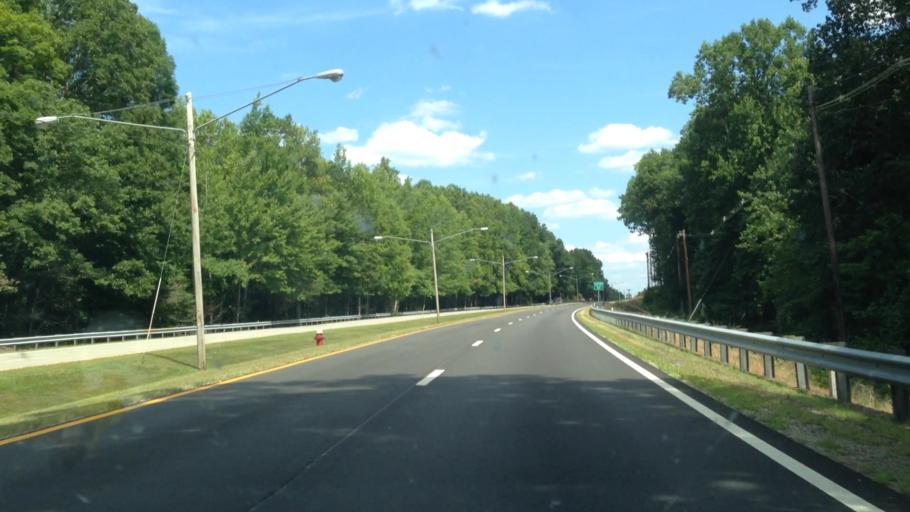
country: US
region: Virginia
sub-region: City of Danville
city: Danville
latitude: 36.5974
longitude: -79.4757
